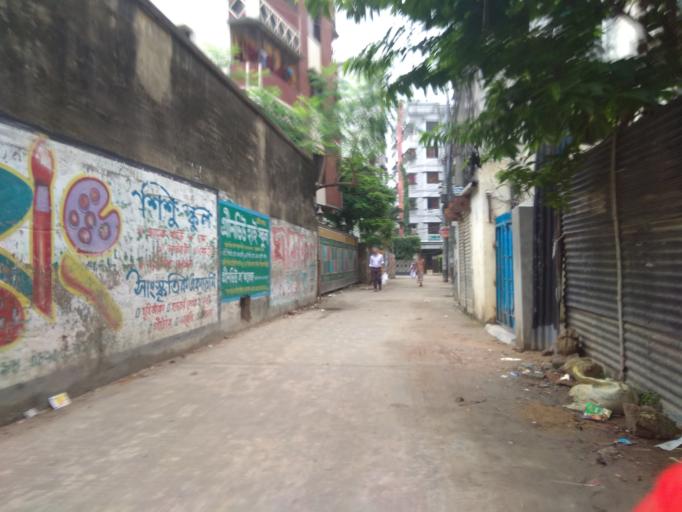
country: BD
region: Dhaka
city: Azimpur
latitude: 23.7964
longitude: 90.3670
